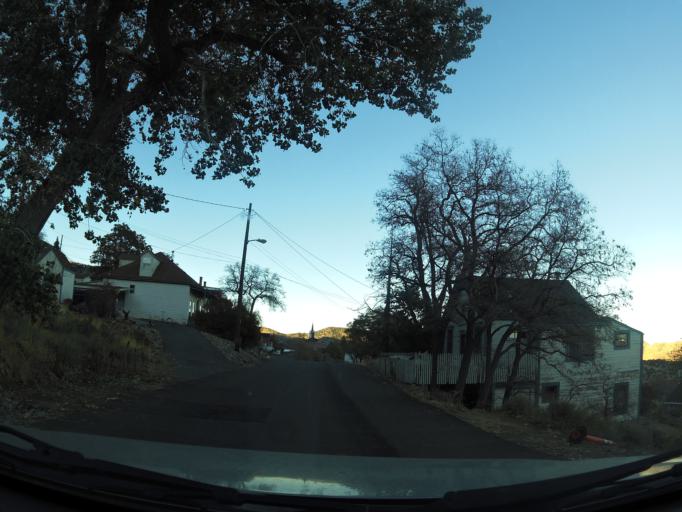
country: US
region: Nevada
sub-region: Storey County
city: Virginia City
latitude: 39.3044
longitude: -119.6515
